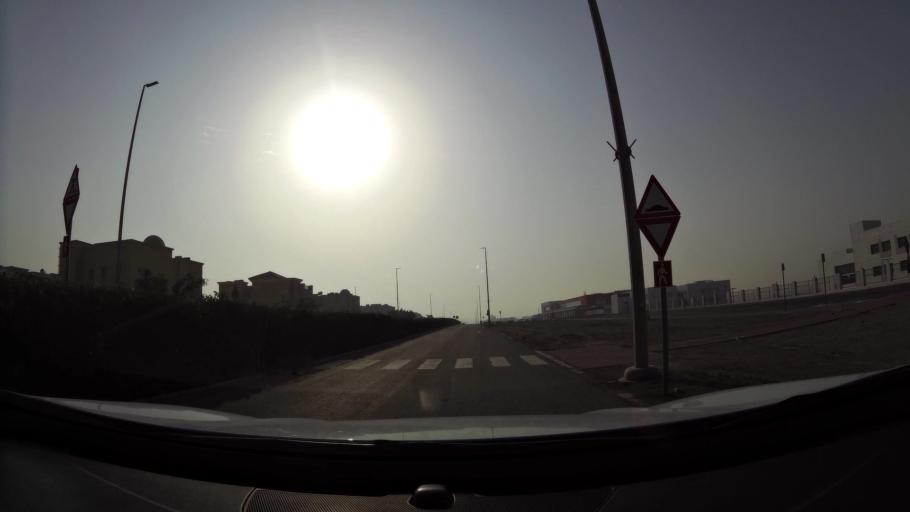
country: AE
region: Abu Dhabi
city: Abu Dhabi
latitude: 24.2954
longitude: 54.6187
